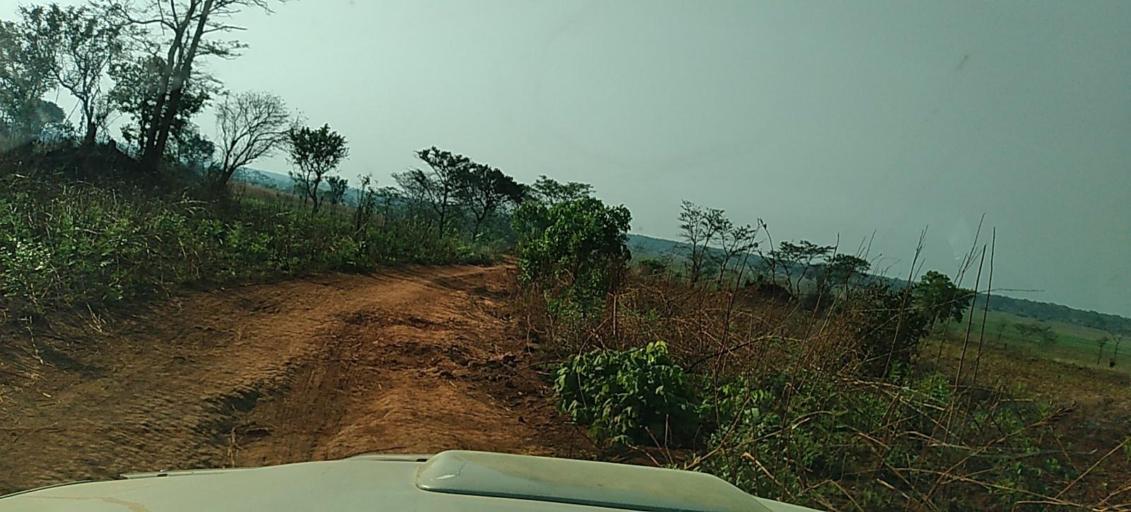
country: ZM
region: North-Western
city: Kasempa
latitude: -13.1817
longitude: 25.9455
